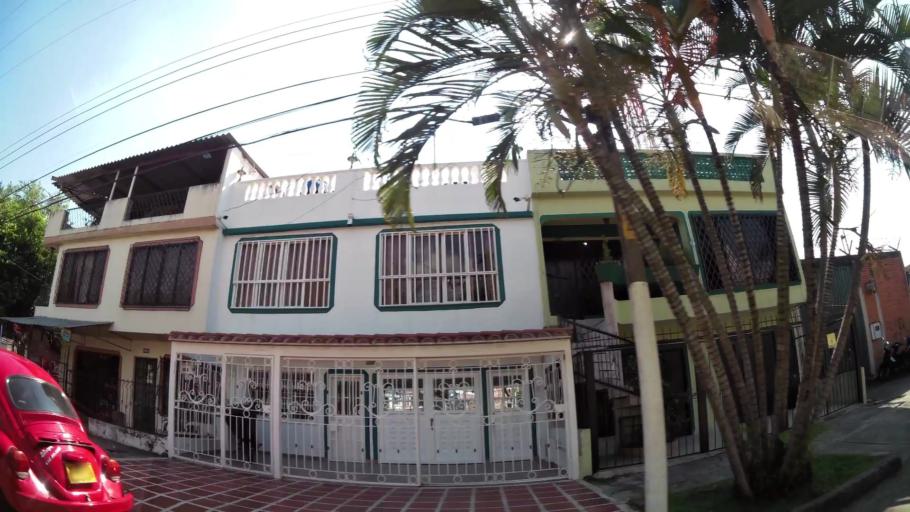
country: CO
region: Valle del Cauca
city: Cali
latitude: 3.4208
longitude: -76.5288
